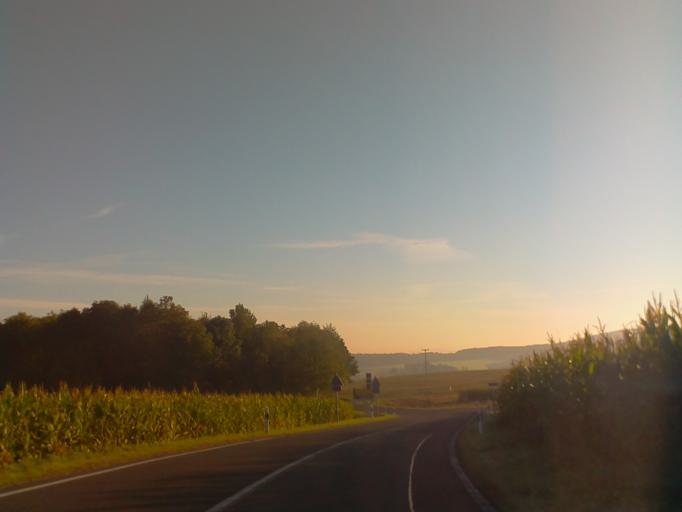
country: DE
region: Thuringia
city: Unterbodnitz
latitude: 50.8067
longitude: 11.6458
